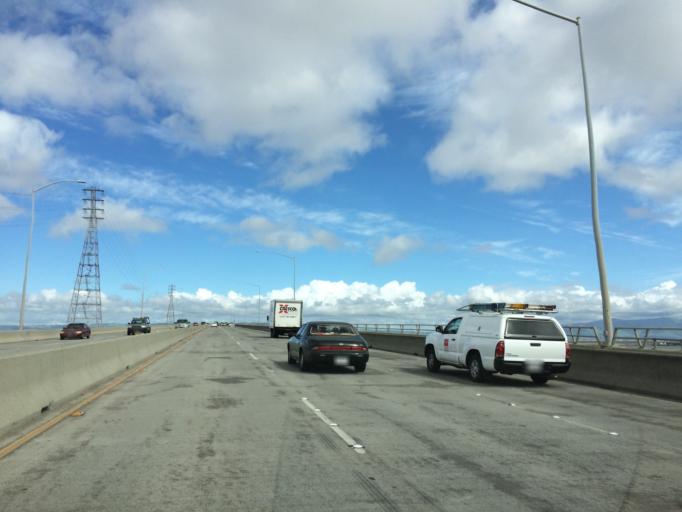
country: US
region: California
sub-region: San Mateo County
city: East Palo Alto
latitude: 37.5006
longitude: -122.1265
